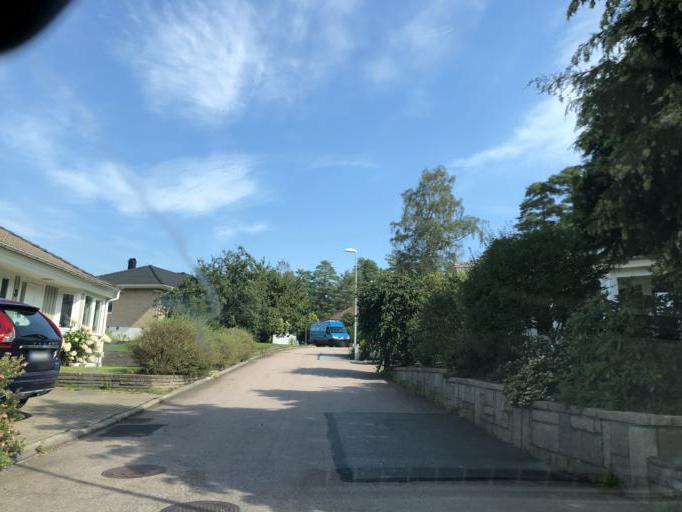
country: SE
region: Vaestra Goetaland
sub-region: Goteborg
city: Goeteborg
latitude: 57.7633
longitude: 11.9665
